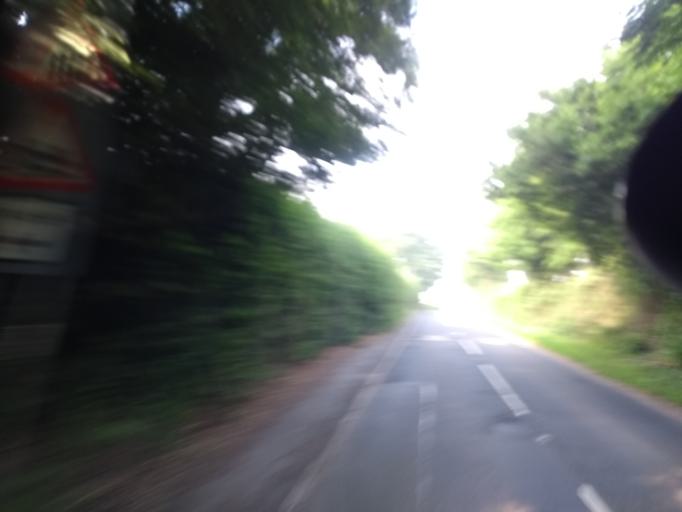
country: GB
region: England
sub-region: Somerset
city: Crewkerne
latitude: 50.8753
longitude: -2.8017
